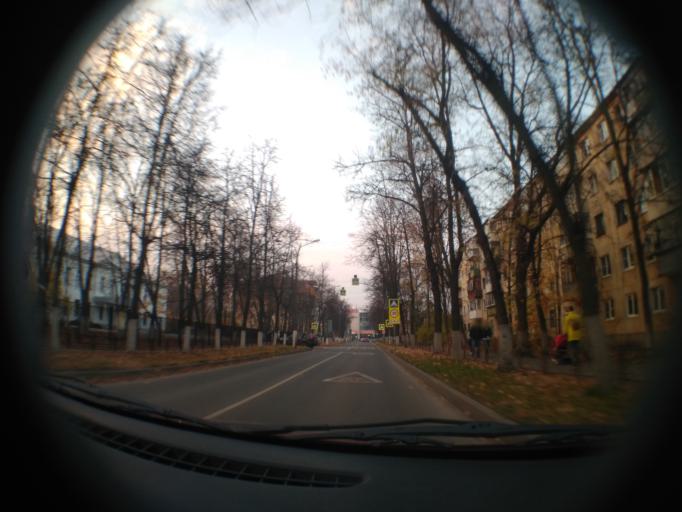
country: RU
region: Moskovskaya
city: Zhukovskiy
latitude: 55.5998
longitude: 38.1162
